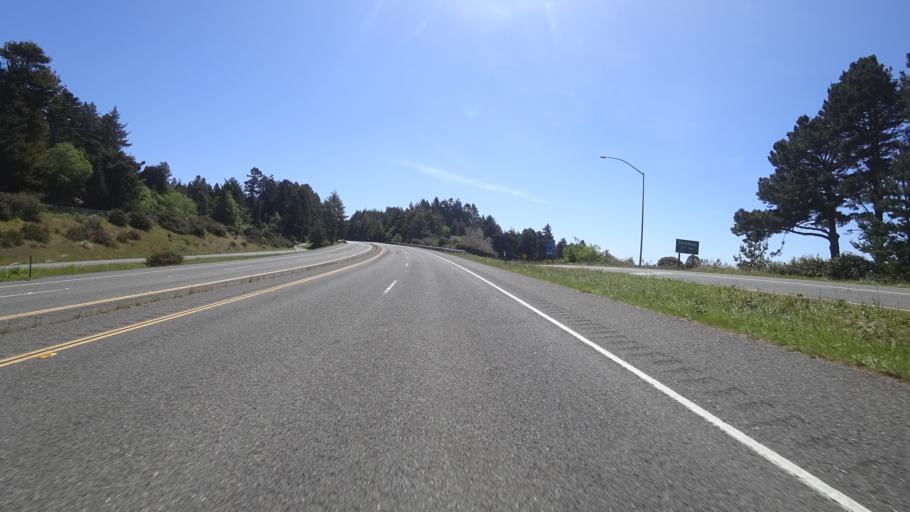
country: US
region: California
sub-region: Humboldt County
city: Westhaven-Moonstone
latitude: 41.0633
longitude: -124.1408
